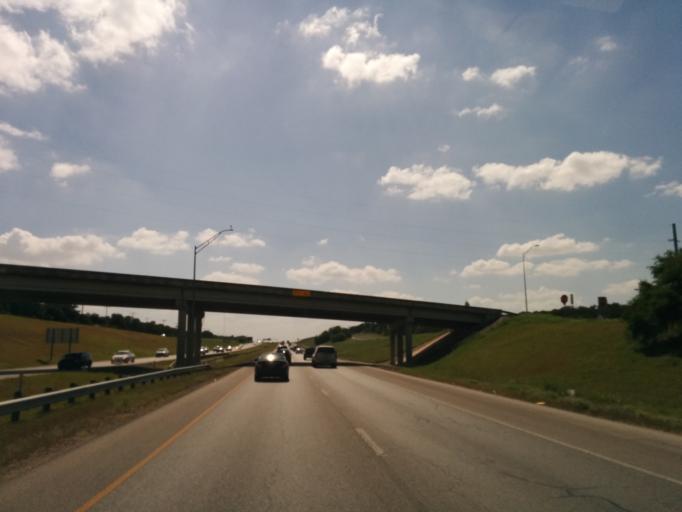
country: US
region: Texas
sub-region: Bexar County
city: Live Oak
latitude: 29.6029
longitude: -98.3653
